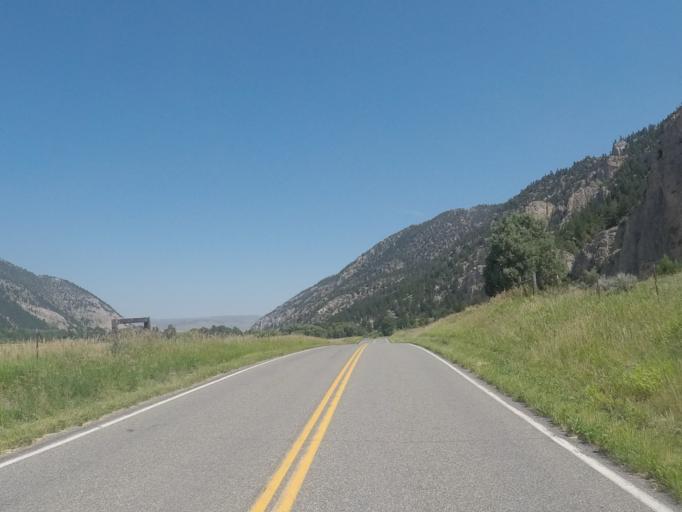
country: US
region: Montana
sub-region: Park County
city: Livingston
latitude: 45.5896
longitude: -110.5609
